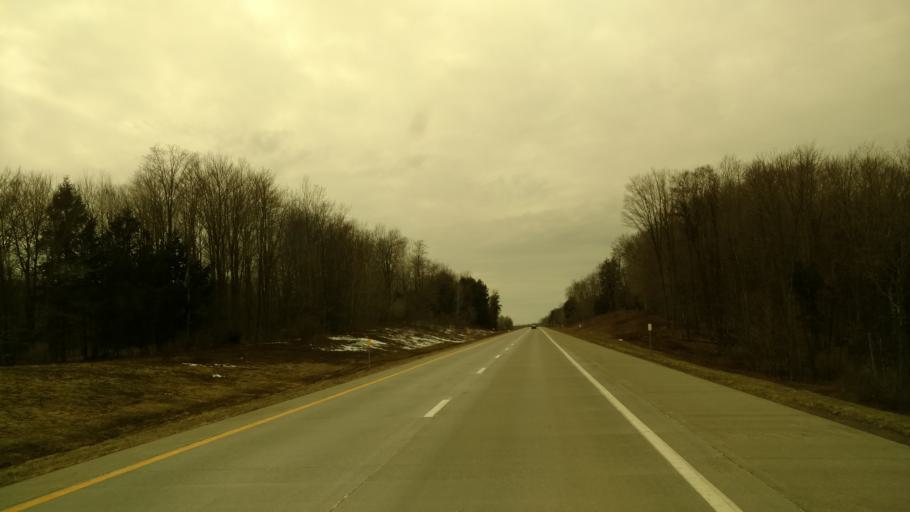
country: US
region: New York
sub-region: Chautauqua County
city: Mayville
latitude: 42.1555
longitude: -79.4552
